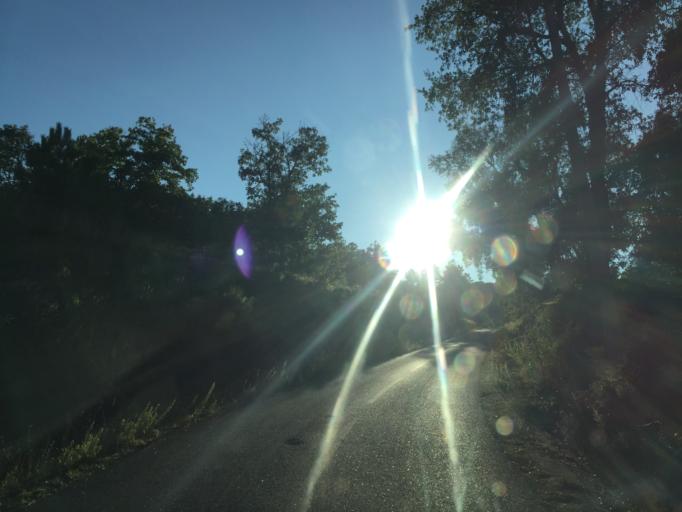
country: PT
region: Portalegre
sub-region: Castelo de Vide
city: Castelo de Vide
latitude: 39.4039
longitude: -7.4448
